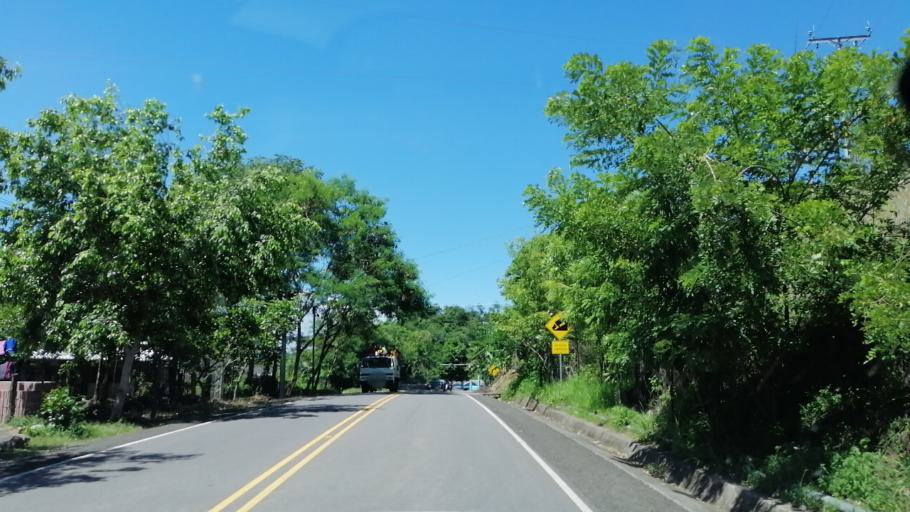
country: SV
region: San Miguel
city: Ciudad Barrios
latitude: 13.8133
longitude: -88.1799
